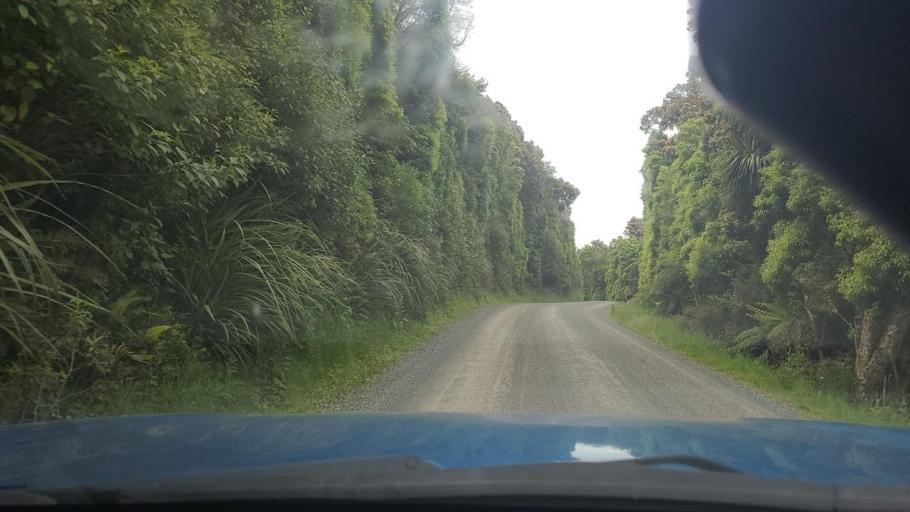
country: NZ
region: Otago
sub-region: Clutha District
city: Papatowai
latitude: -46.4835
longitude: 169.1510
